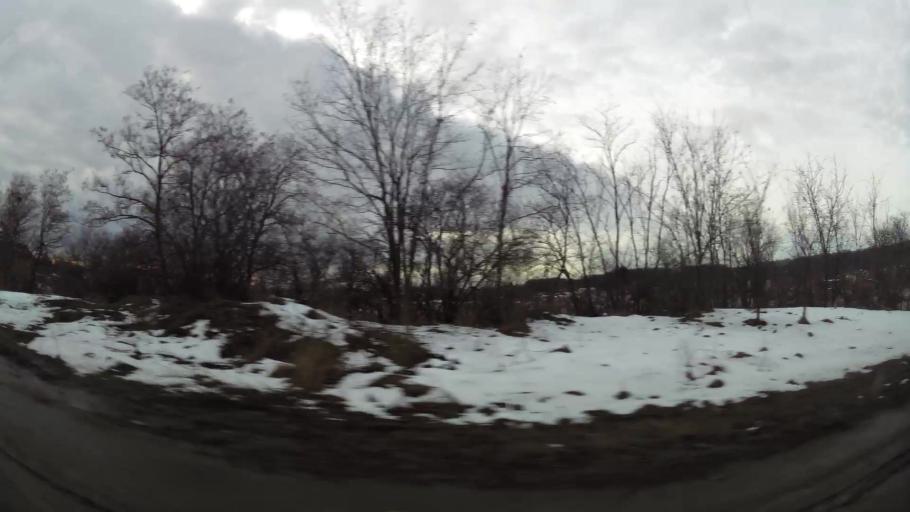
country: RS
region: Central Serbia
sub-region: Belgrade
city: Rakovica
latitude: 44.7234
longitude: 20.4958
